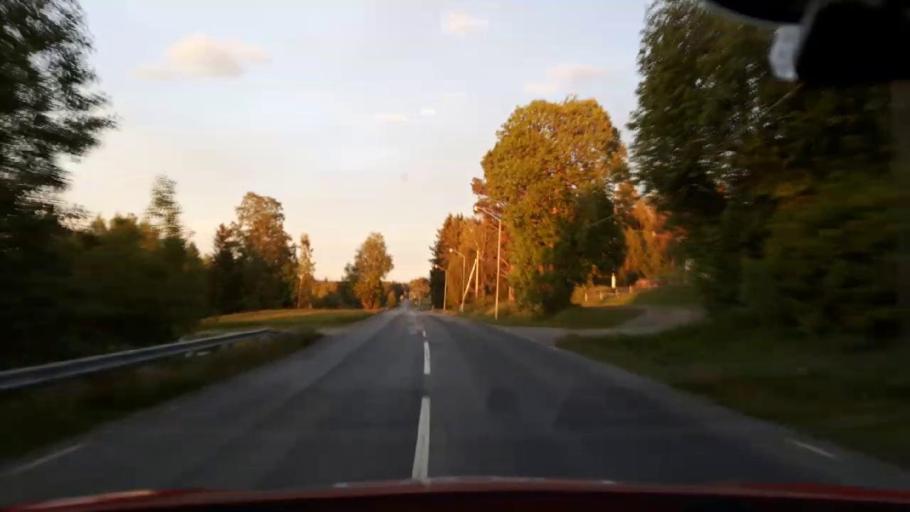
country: SE
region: Jaemtland
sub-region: OEstersunds Kommun
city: Ostersund
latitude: 63.1367
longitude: 14.6358
